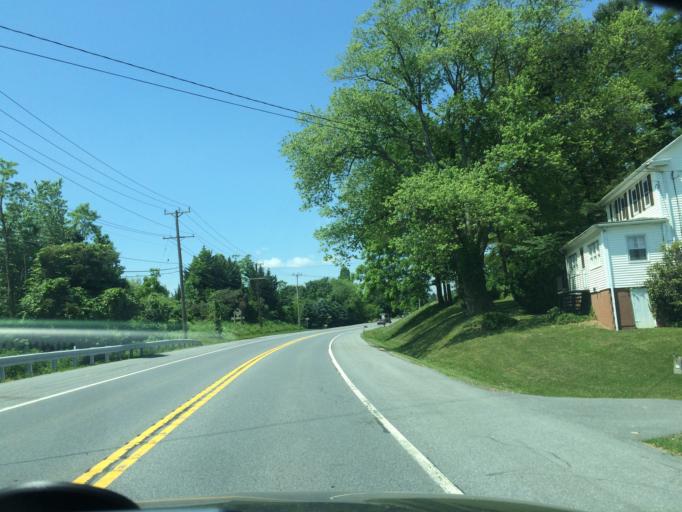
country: US
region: Maryland
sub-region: Carroll County
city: Eldersburg
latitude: 39.4661
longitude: -76.9305
